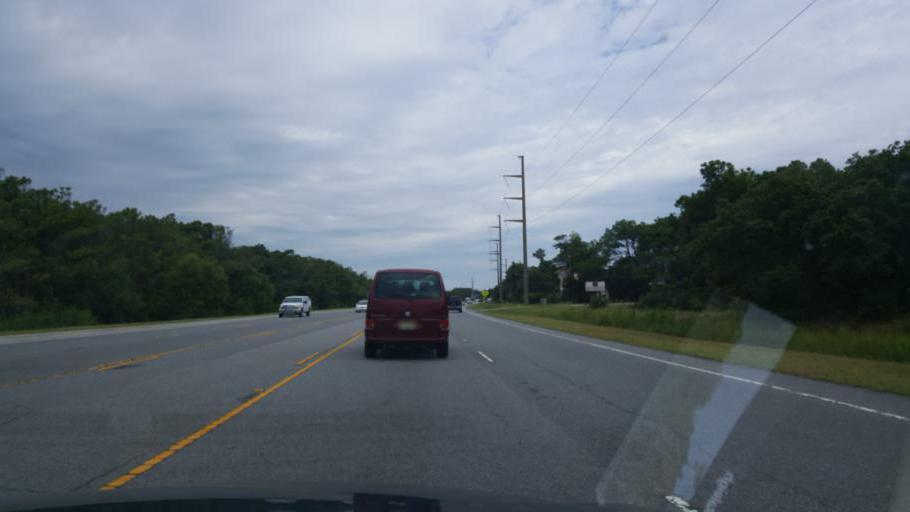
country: US
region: North Carolina
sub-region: Dare County
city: Nags Head
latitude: 35.9713
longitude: -75.6368
